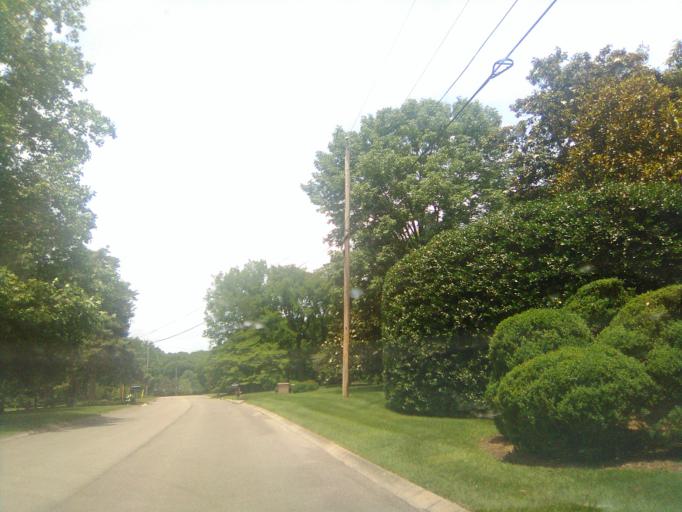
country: US
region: Tennessee
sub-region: Davidson County
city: Belle Meade
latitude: 36.0840
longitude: -86.8564
